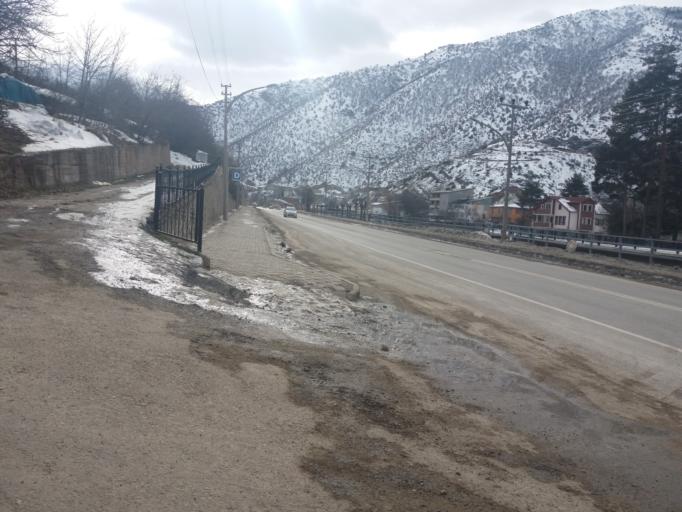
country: TR
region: Gumushane
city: Gumushkhane
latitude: 40.4426
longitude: 39.5035
